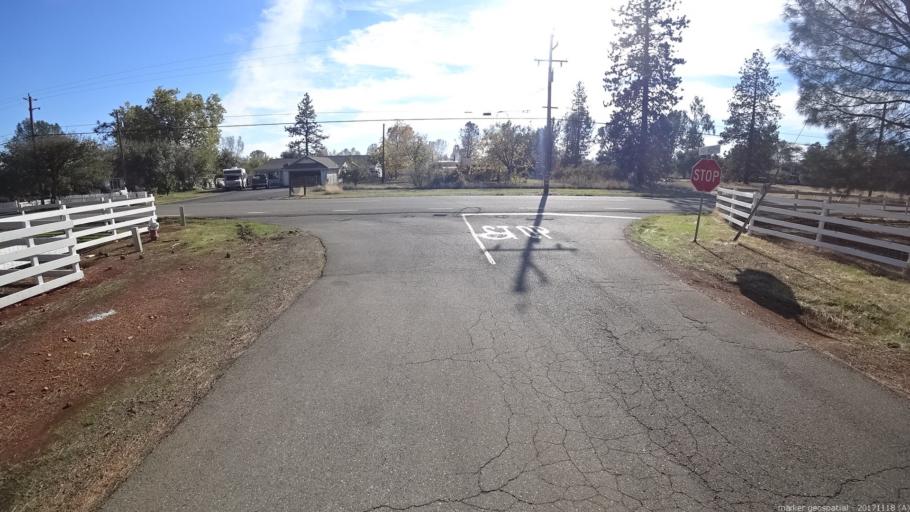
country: US
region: California
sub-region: Shasta County
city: Redding
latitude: 40.4782
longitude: -122.4434
